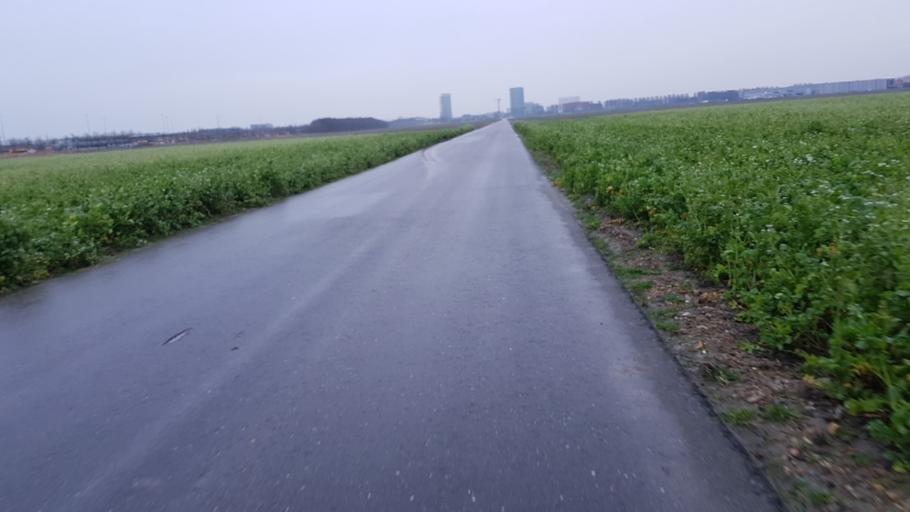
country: NL
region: North Holland
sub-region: Gemeente Haarlemmermeer
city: Hoofddorp
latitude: 52.2784
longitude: 4.6792
